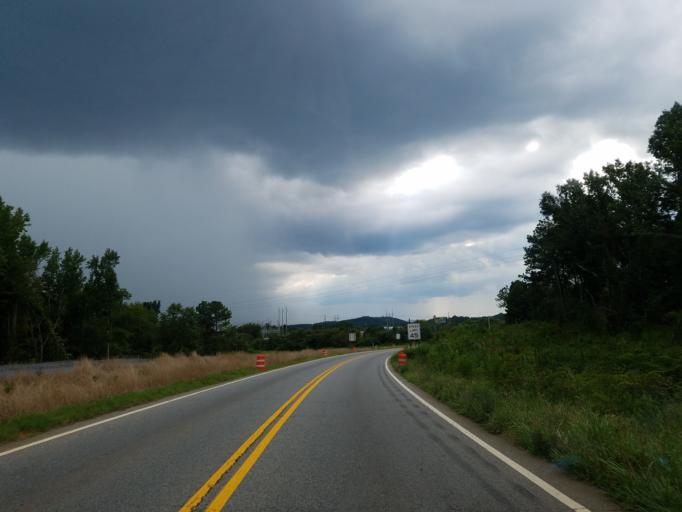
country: US
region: Georgia
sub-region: Floyd County
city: Shannon
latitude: 34.3659
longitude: -85.0468
